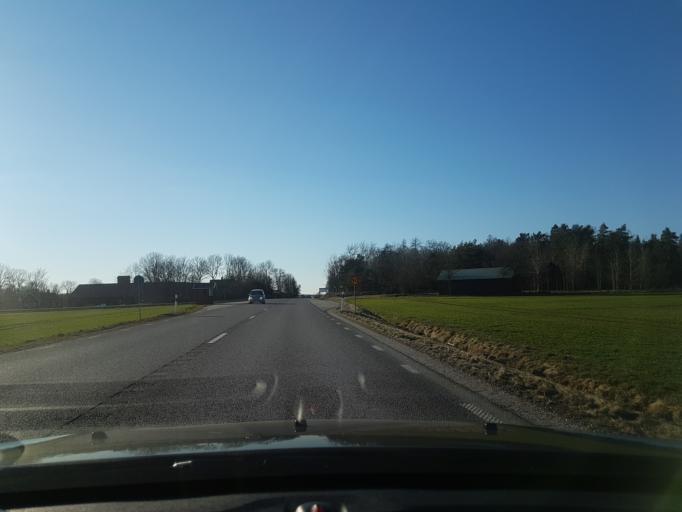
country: SE
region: Uppsala
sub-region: Enkopings Kommun
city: Orsundsbro
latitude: 59.8743
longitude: 17.2940
